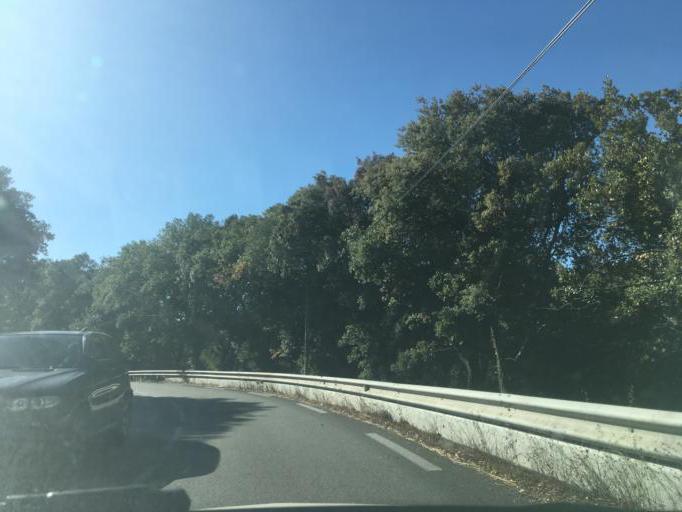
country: FR
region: Provence-Alpes-Cote d'Azur
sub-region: Departement du Var
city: La Garde-Freinet
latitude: 43.3211
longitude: 6.4722
